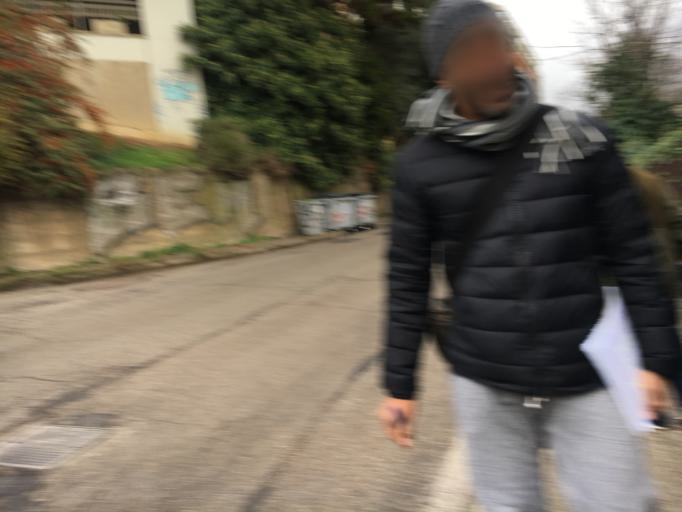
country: IT
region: Umbria
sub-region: Provincia di Perugia
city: Perugia
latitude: 43.1155
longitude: 12.3758
